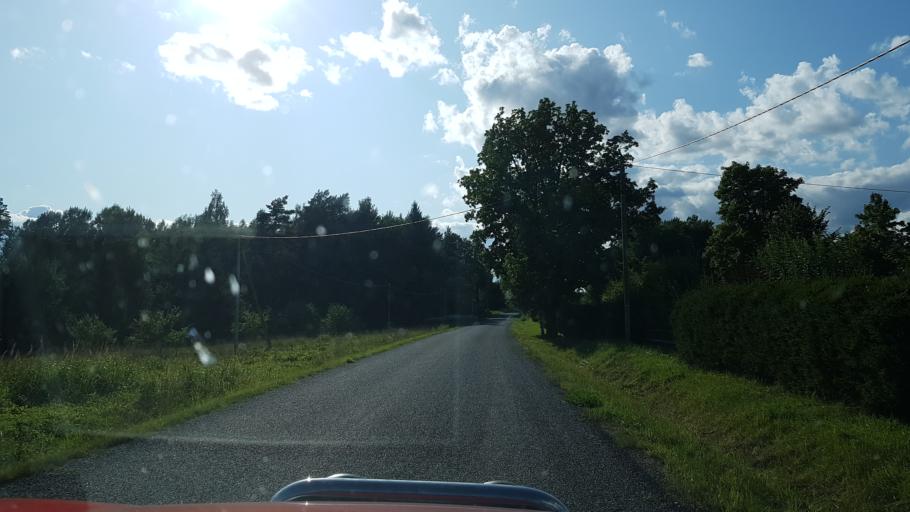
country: EE
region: Vorumaa
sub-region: Voru linn
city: Voru
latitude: 57.9262
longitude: 27.0970
